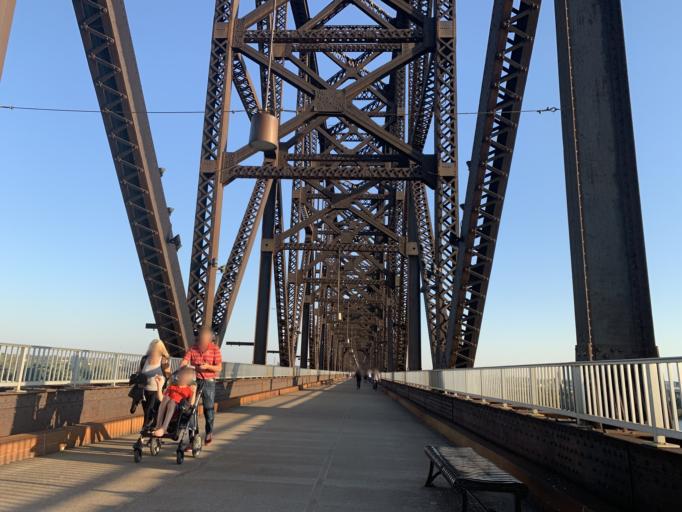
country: US
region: Indiana
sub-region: Clark County
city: Jeffersonville
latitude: 38.2679
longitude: -85.7408
